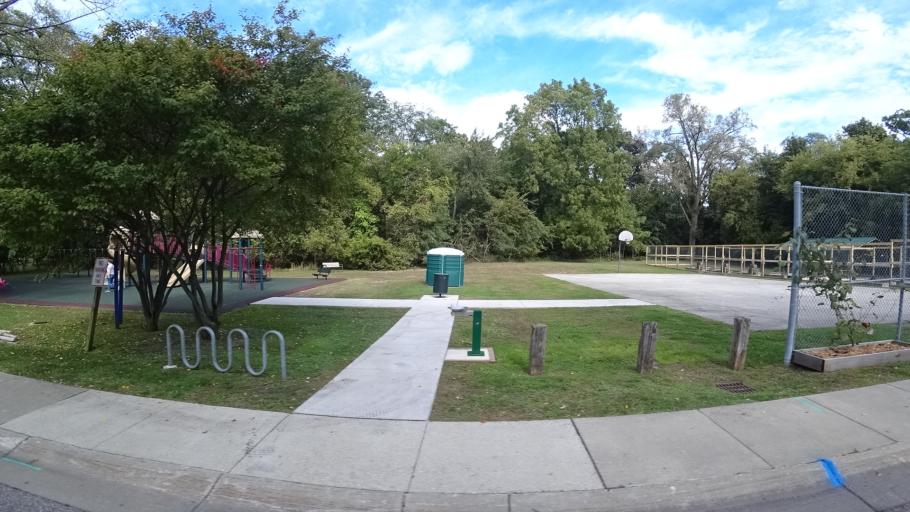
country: US
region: Indiana
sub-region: LaPorte County
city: Michigan City
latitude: 41.7143
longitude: -86.8762
